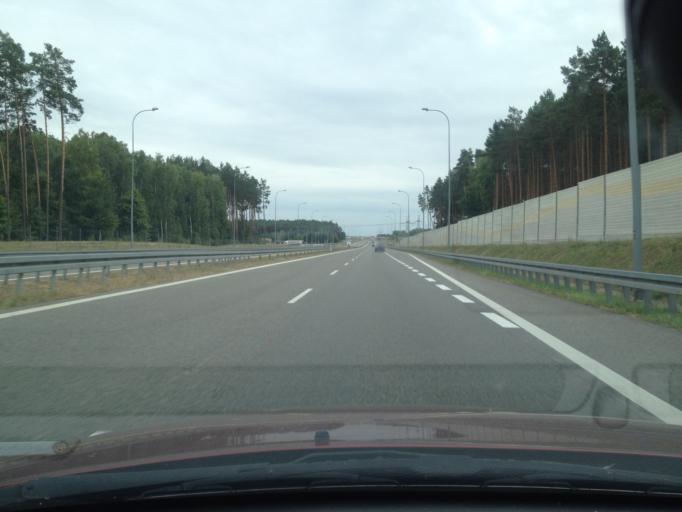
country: PL
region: Lubusz
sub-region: Powiat gorzowski
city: Jenin
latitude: 52.7913
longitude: 15.1161
